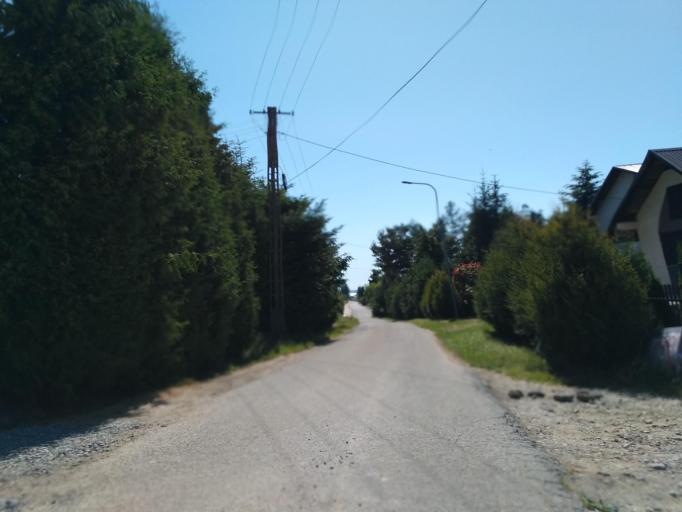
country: PL
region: Subcarpathian Voivodeship
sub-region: Powiat krosnienski
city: Korczyna
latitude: 49.7266
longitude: 21.7818
